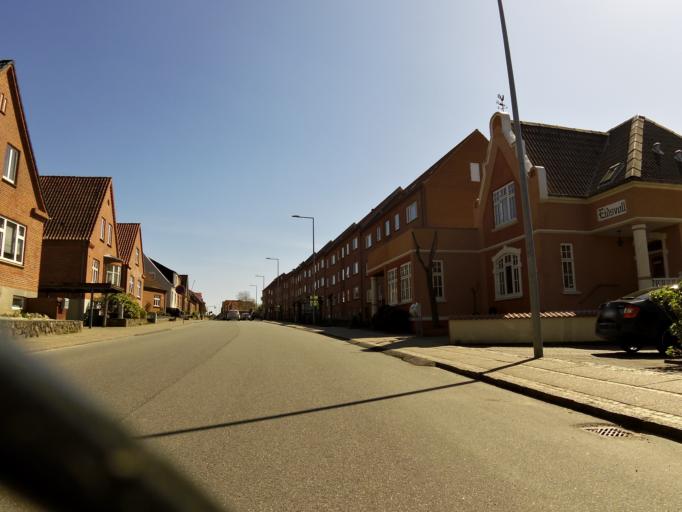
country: DK
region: Central Jutland
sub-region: Struer Kommune
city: Struer
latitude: 56.4888
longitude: 8.5994
